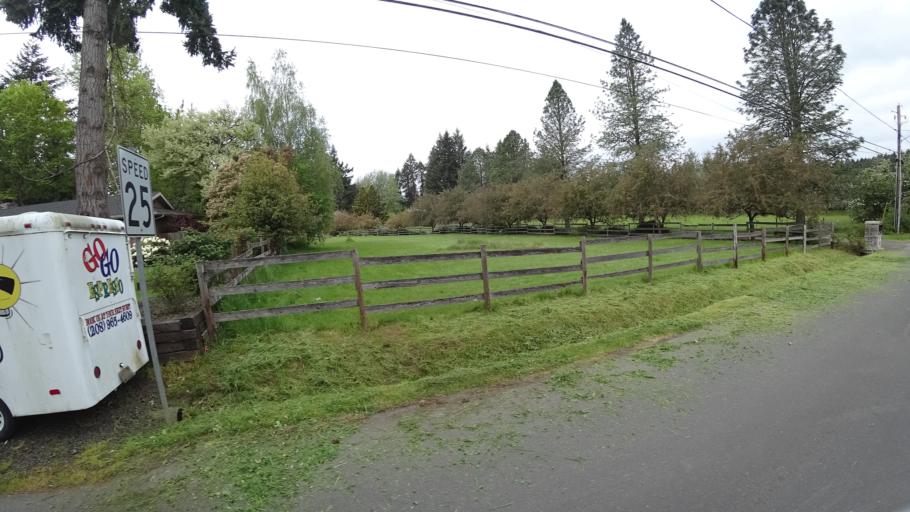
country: US
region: Oregon
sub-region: Washington County
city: Hillsboro
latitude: 45.5314
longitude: -123.0005
